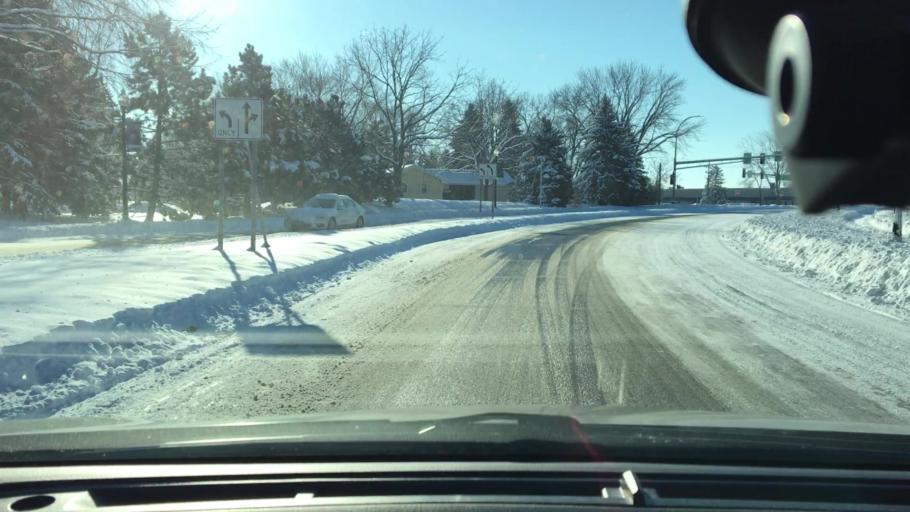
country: US
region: Minnesota
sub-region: Hennepin County
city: Plymouth
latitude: 45.0167
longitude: -93.4720
